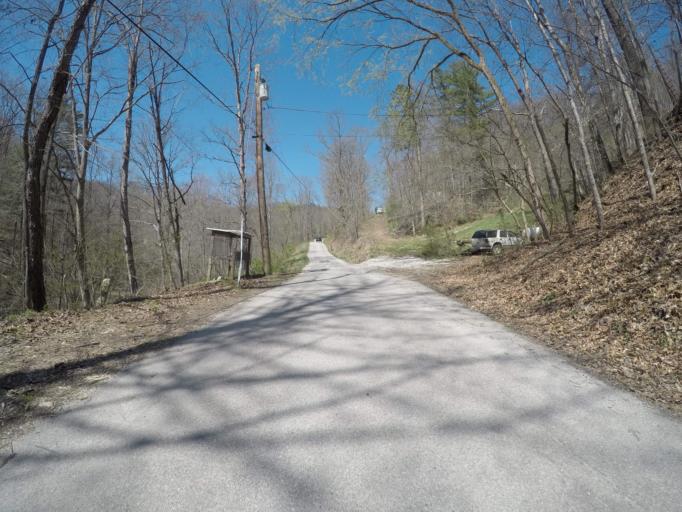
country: US
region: West Virginia
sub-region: Kanawha County
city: Charleston
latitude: 38.4071
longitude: -81.5889
